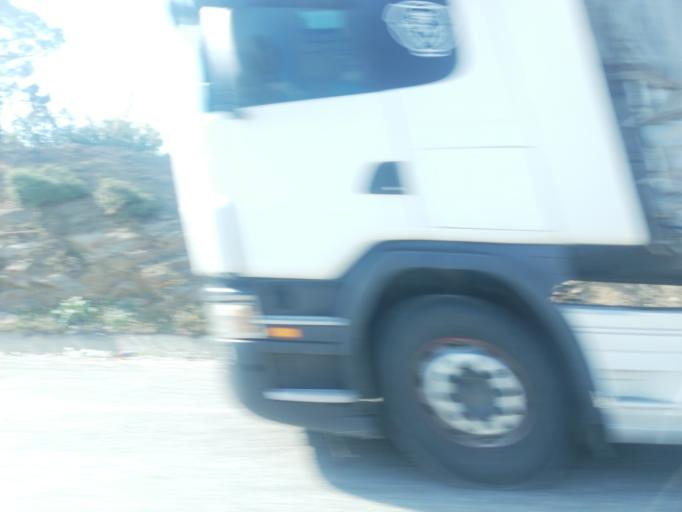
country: TR
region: Manisa
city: Sarigol
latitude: 38.2148
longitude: 28.6609
